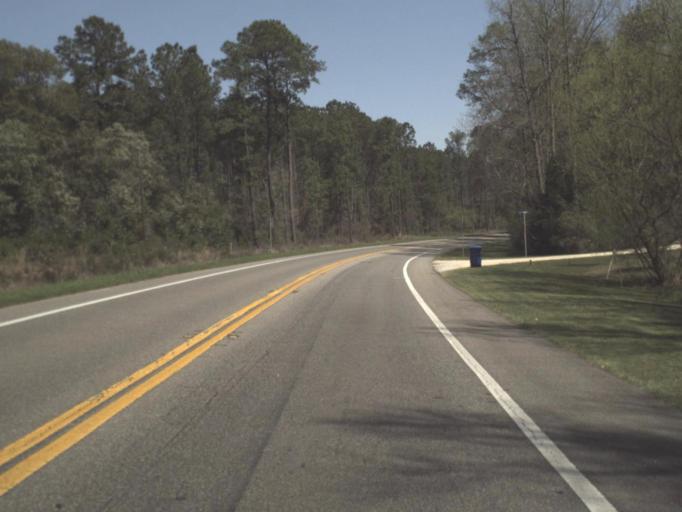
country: US
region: Florida
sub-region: Calhoun County
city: Blountstown
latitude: 30.4368
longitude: -85.1828
